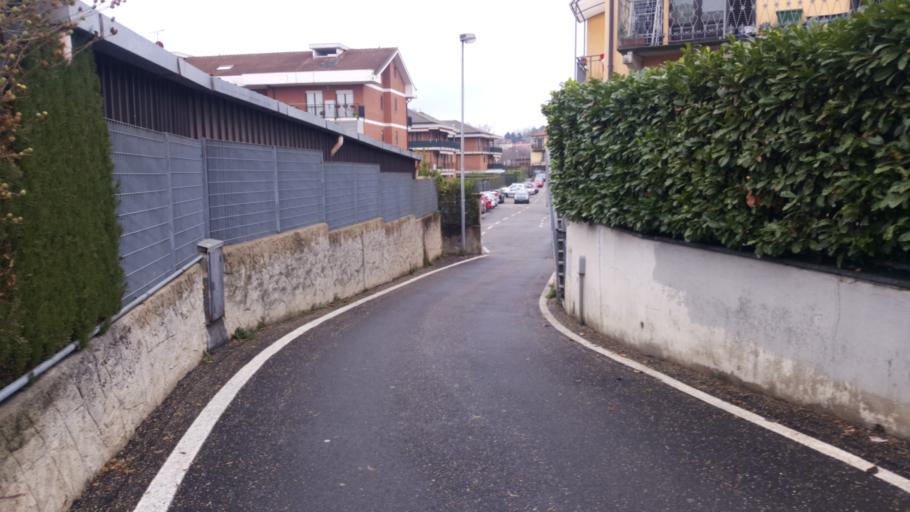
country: IT
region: Piedmont
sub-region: Provincia di Torino
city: Alpignano
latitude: 45.0909
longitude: 7.5242
